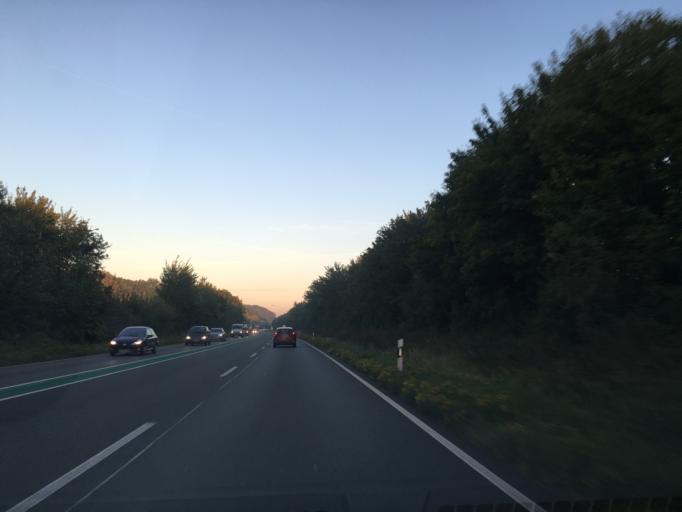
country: DE
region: North Rhine-Westphalia
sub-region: Regierungsbezirk Munster
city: Laer
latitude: 52.0990
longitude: 7.4012
